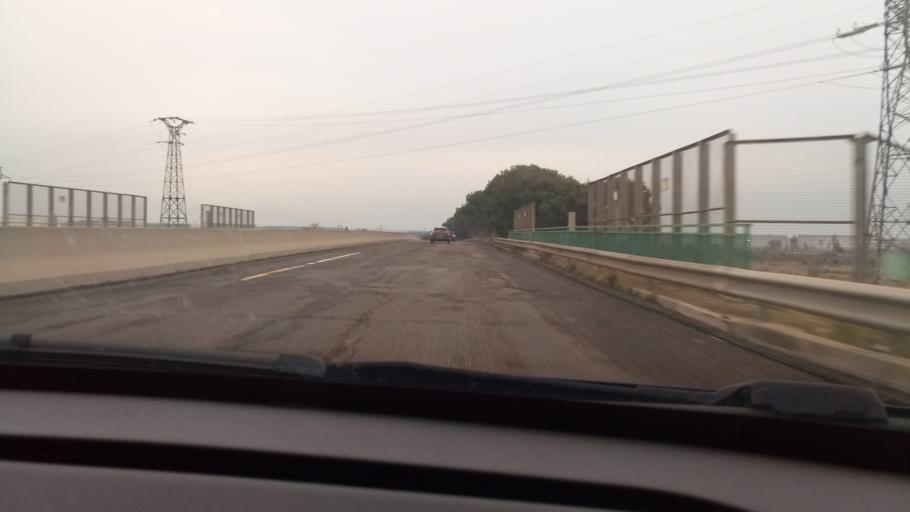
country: FR
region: Provence-Alpes-Cote d'Azur
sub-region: Departement des Bouches-du-Rhone
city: Fos-sur-Mer
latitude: 43.4744
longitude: 4.9020
